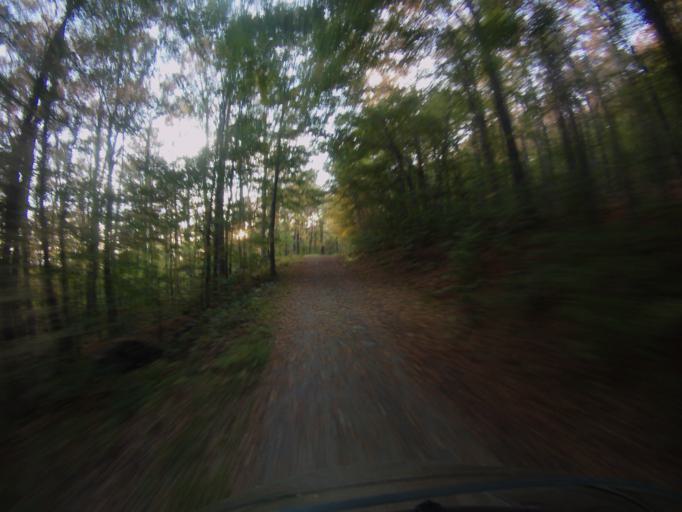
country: US
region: Vermont
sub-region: Addison County
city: Bristol
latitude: 44.0922
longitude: -72.9433
